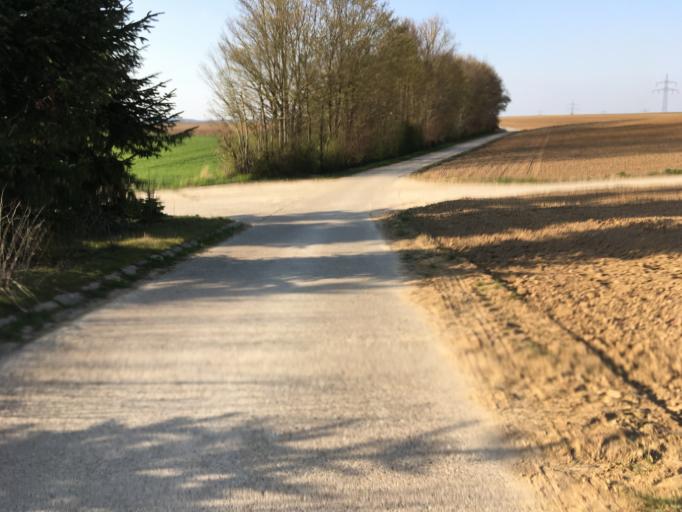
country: DE
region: Baden-Wuerttemberg
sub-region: Regierungsbezirk Stuttgart
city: Nordheim
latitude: 49.0825
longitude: 9.1167
